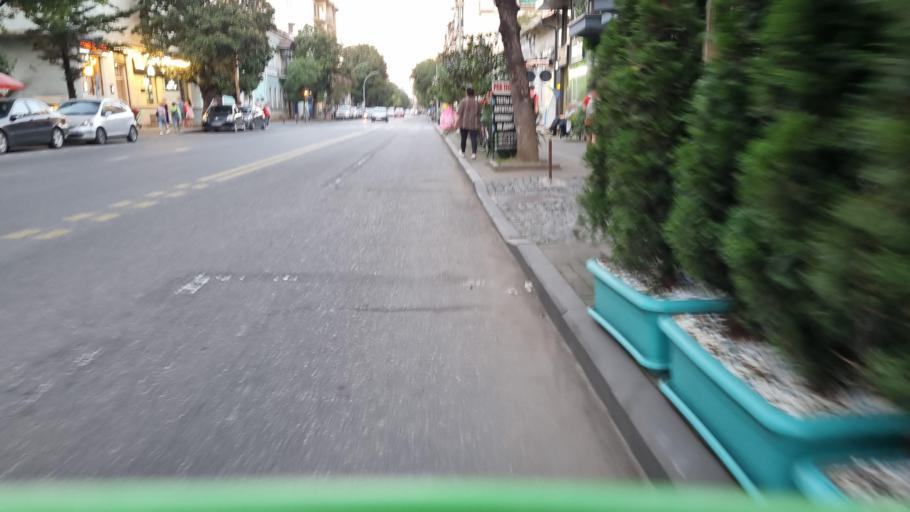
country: GE
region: Ajaria
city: Batumi
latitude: 41.6466
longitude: 41.6300
